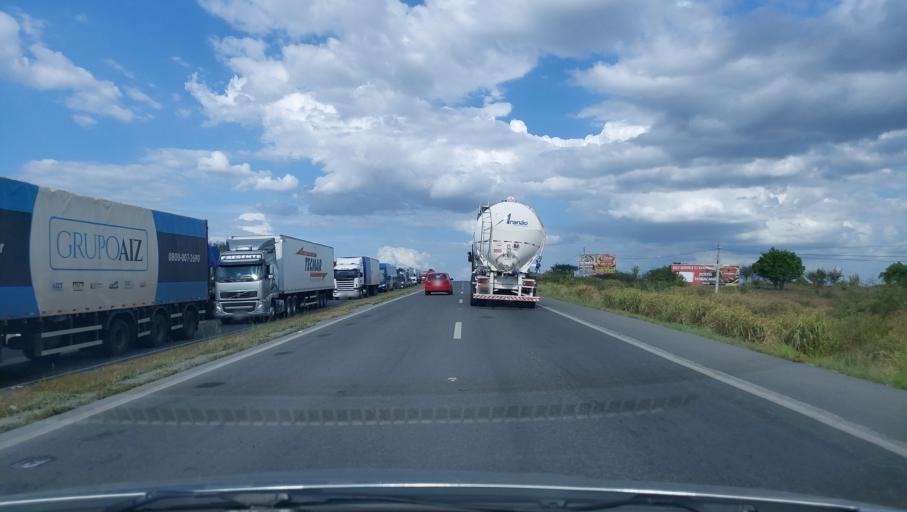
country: BR
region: Bahia
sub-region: Castro Alves
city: Castro Alves
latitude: -12.5776
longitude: -39.5077
